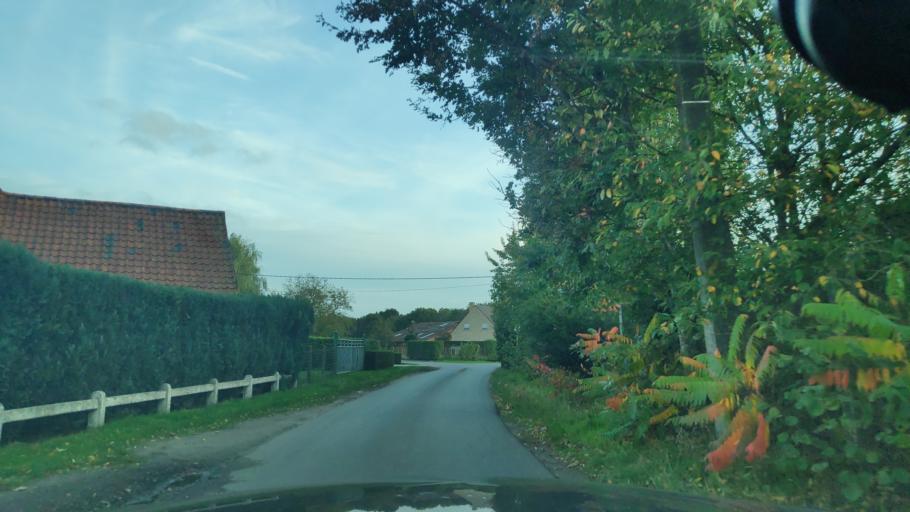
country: BE
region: Flanders
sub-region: Provincie Oost-Vlaanderen
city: Aalter
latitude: 51.1104
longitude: 3.4698
